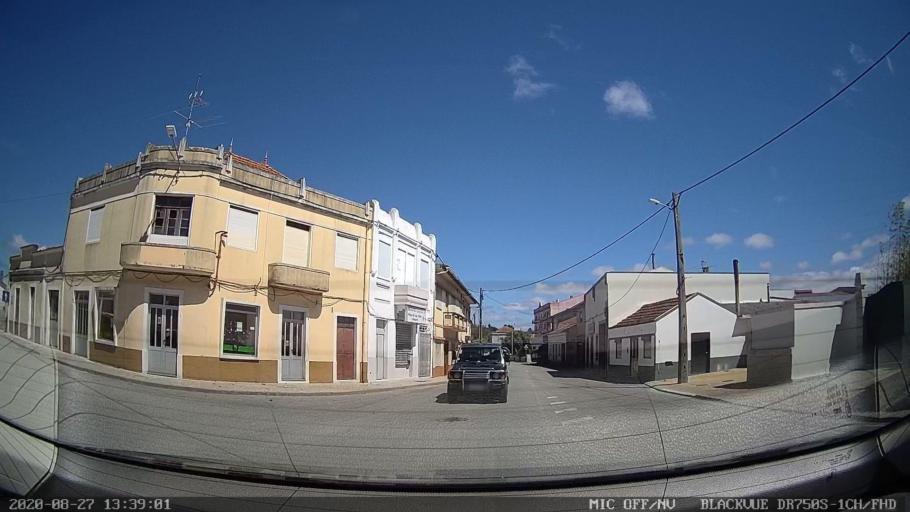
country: PT
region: Coimbra
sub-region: Mira
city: Mira
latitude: 40.4436
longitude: -8.7283
